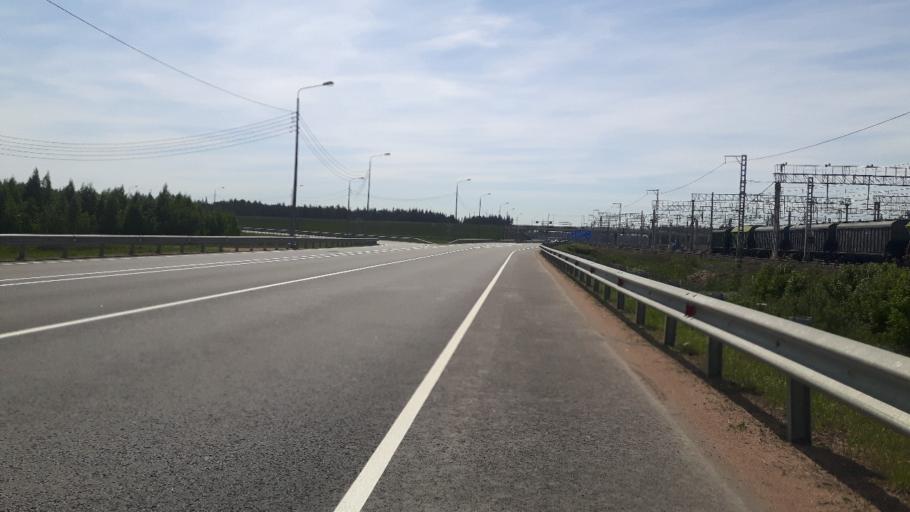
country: RU
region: Leningrad
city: Vistino
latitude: 59.6661
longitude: 28.4339
